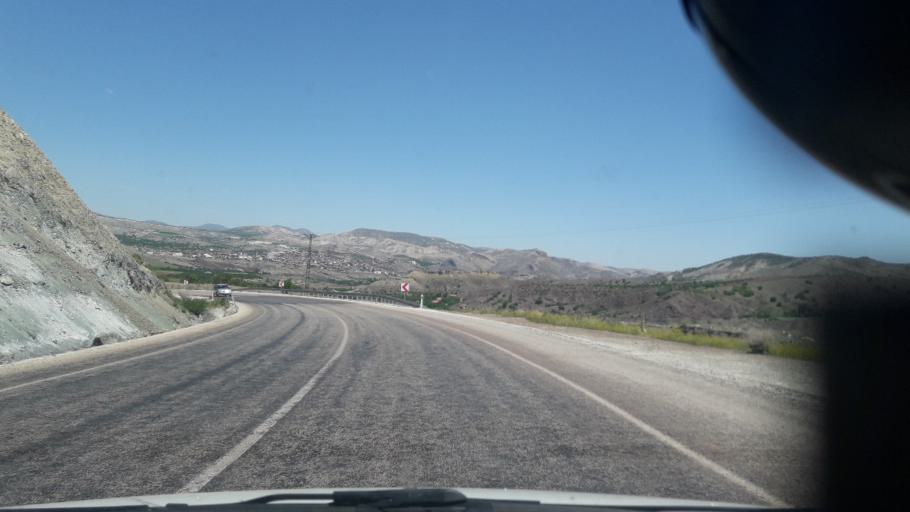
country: TR
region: Malatya
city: Hekimhan
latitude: 38.8209
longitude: 37.8804
